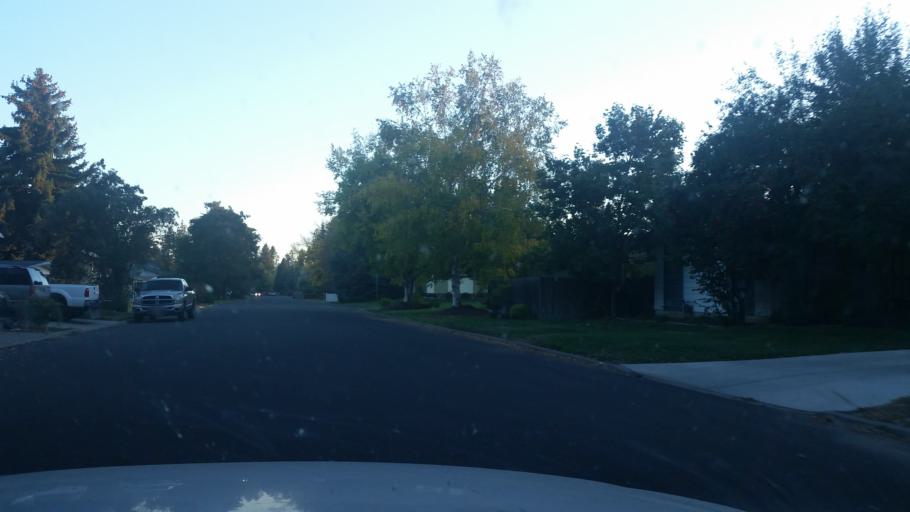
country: US
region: Washington
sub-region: Spokane County
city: Cheney
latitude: 47.4988
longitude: -117.5713
